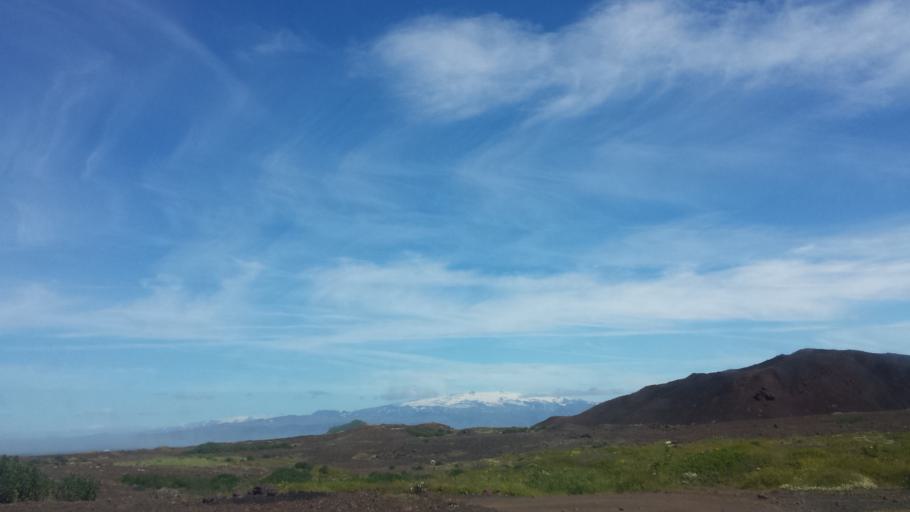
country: IS
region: South
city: Vestmannaeyjar
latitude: 63.4391
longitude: -20.2455
